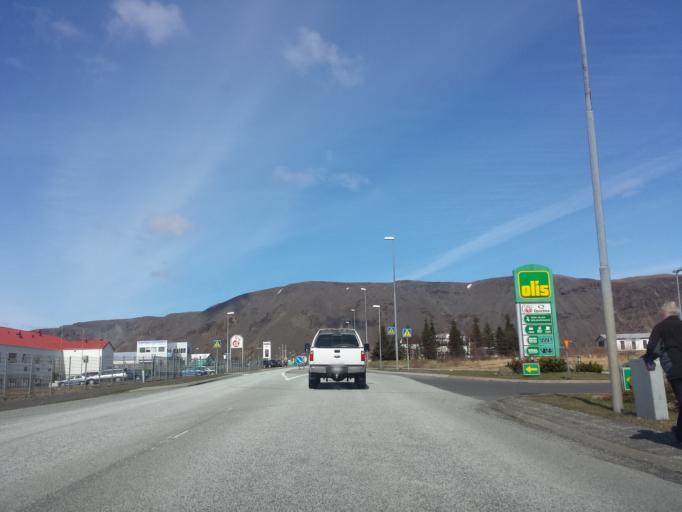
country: IS
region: South
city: Selfoss
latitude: 63.9437
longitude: -21.0086
